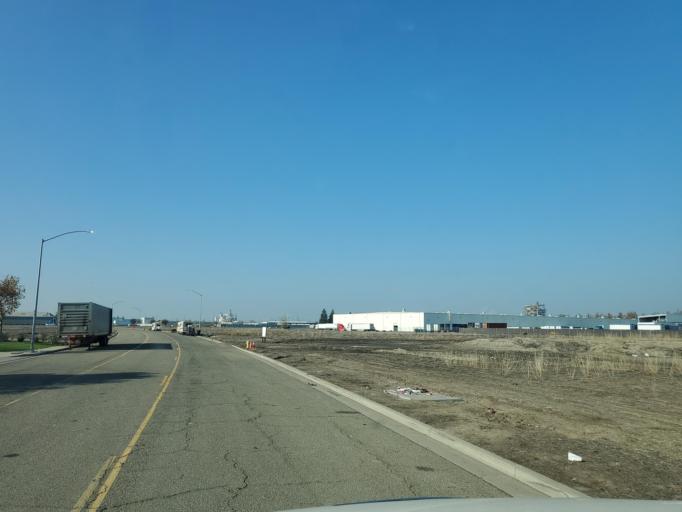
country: US
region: California
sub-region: San Joaquin County
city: Kennedy
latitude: 37.9080
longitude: -121.2531
